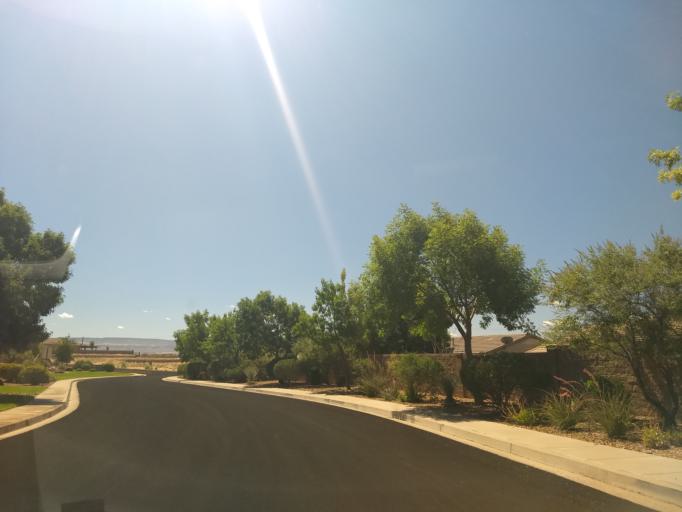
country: US
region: Utah
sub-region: Washington County
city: Washington
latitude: 37.1402
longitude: -113.4695
